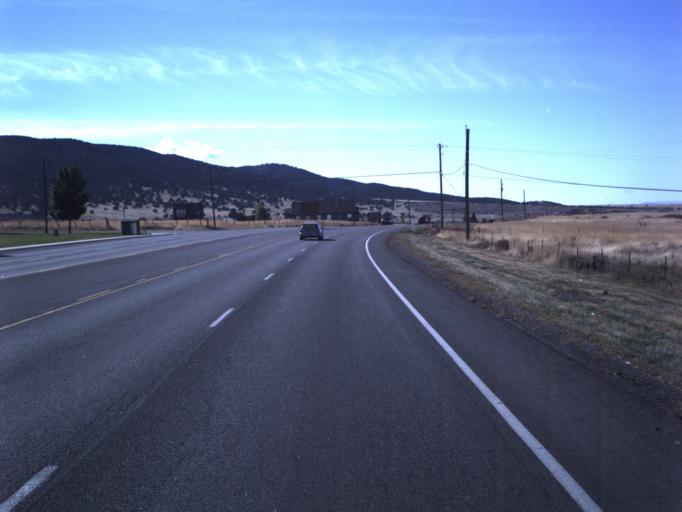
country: US
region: Utah
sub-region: Juab County
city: Nephi
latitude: 39.6910
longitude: -111.8362
